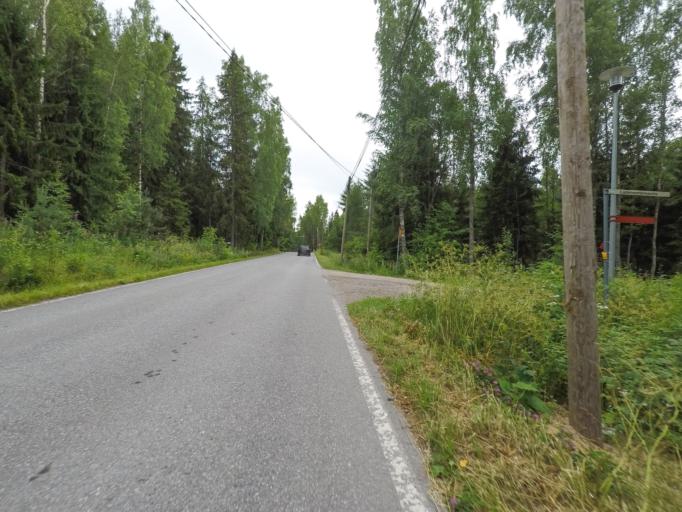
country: FI
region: Uusimaa
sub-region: Helsinki
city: Karjalohja
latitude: 60.2552
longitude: 23.7411
